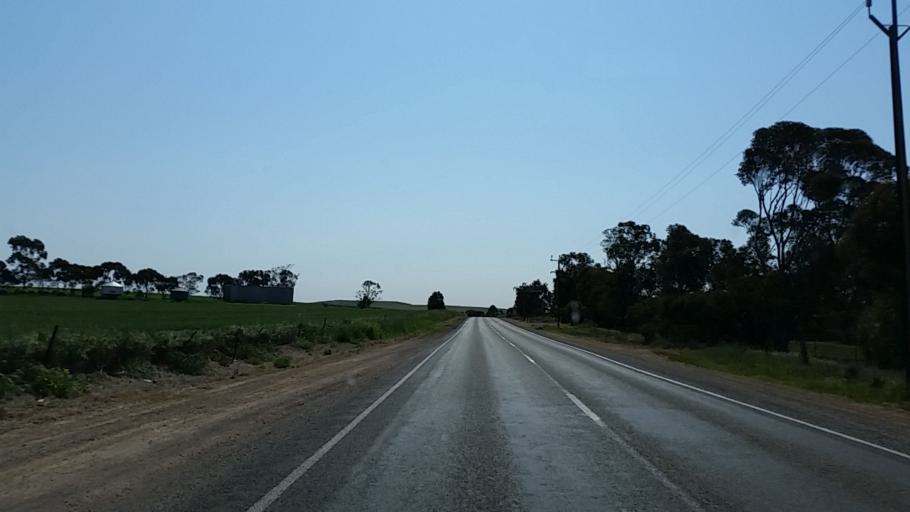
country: AU
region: South Australia
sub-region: Port Pirie City and Dists
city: Crystal Brook
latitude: -33.2570
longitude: 138.3589
